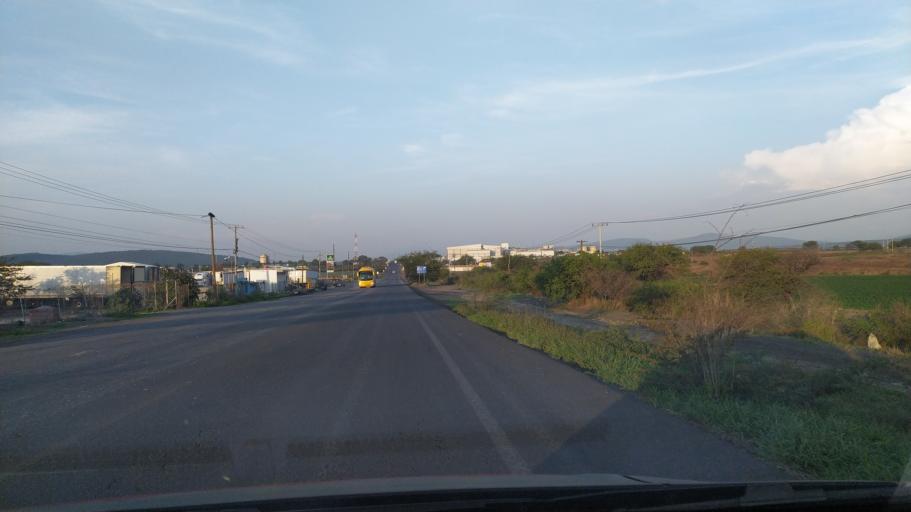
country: MX
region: Michoacan
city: Vistahermosa de Negrete
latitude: 20.2671
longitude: -102.4575
